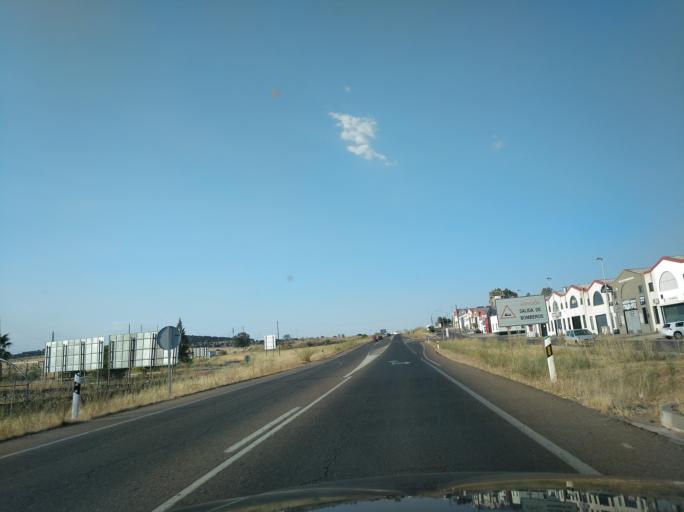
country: ES
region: Extremadura
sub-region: Provincia de Badajoz
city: Olivenza
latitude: 38.6946
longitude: -7.0911
